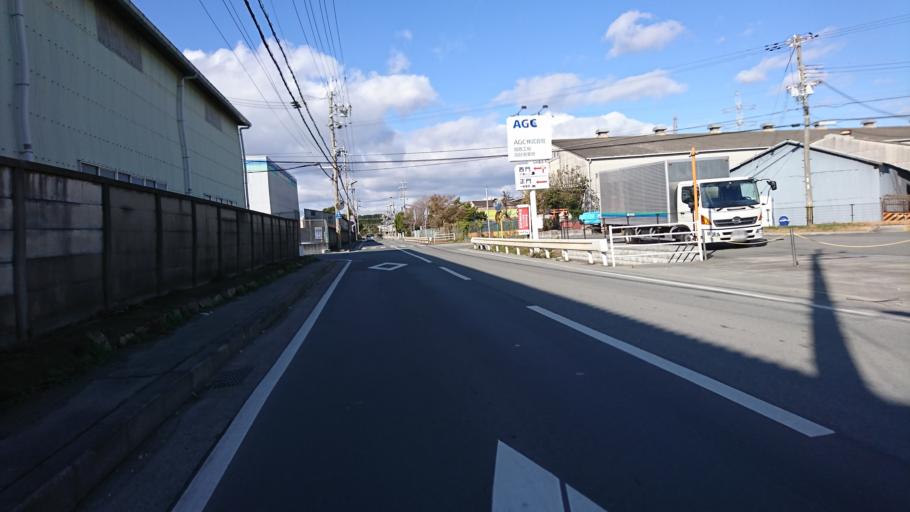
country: JP
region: Hyogo
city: Kakogawacho-honmachi
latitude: 34.7673
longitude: 134.7740
